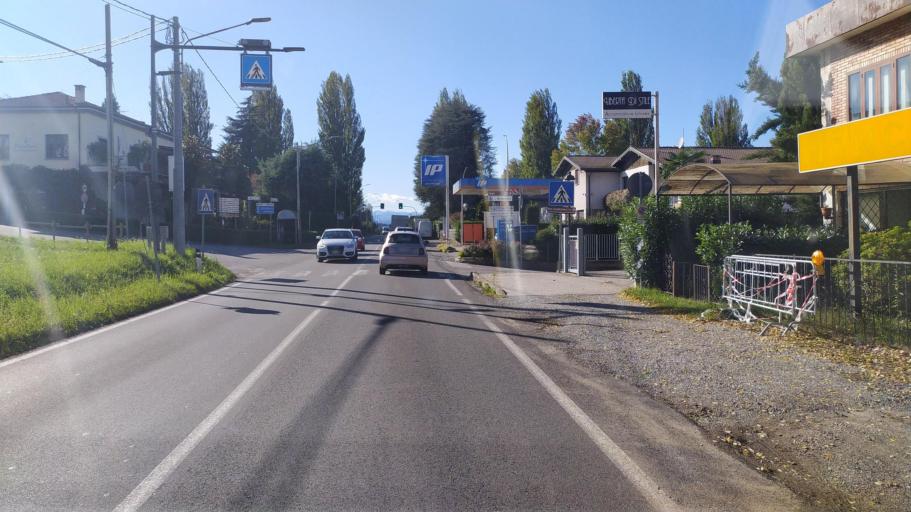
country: IT
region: Lombardy
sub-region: Provincia di Varese
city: Bodio
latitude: 45.7906
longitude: 8.7541
